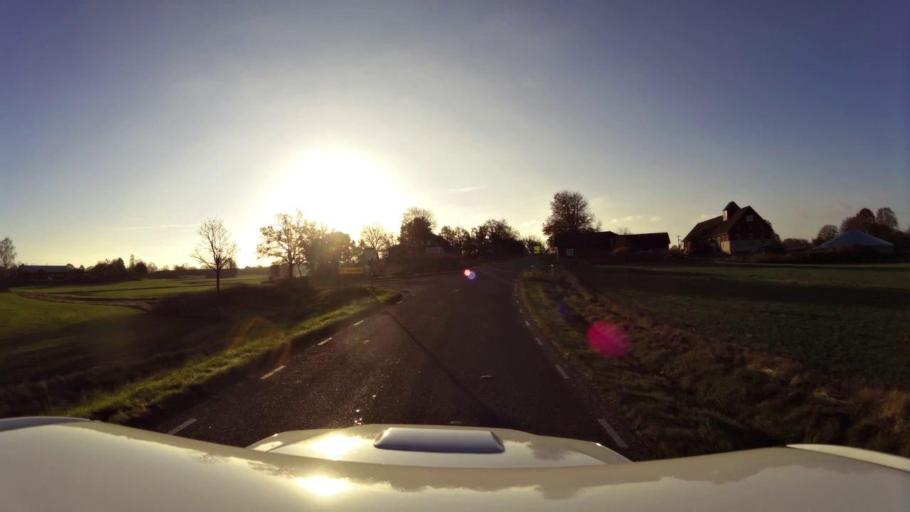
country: SE
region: OEstergoetland
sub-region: Linkopings Kommun
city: Linghem
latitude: 58.4800
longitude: 15.7570
